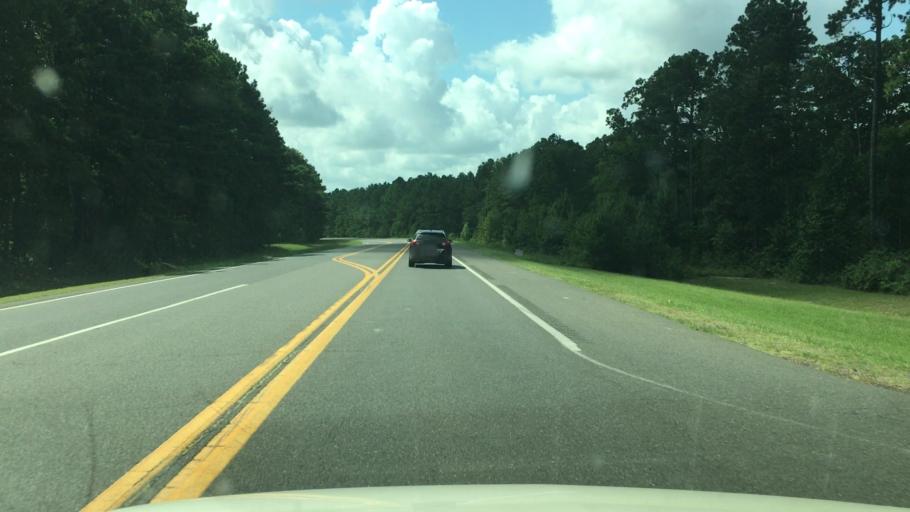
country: US
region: Arkansas
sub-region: Clark County
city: Arkadelphia
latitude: 34.2197
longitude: -93.0866
